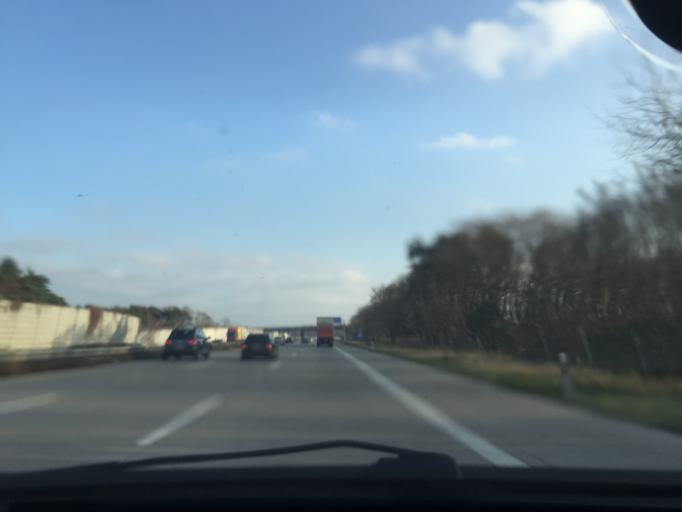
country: DE
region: Saxony-Anhalt
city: Schermen
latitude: 52.2261
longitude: 11.8165
